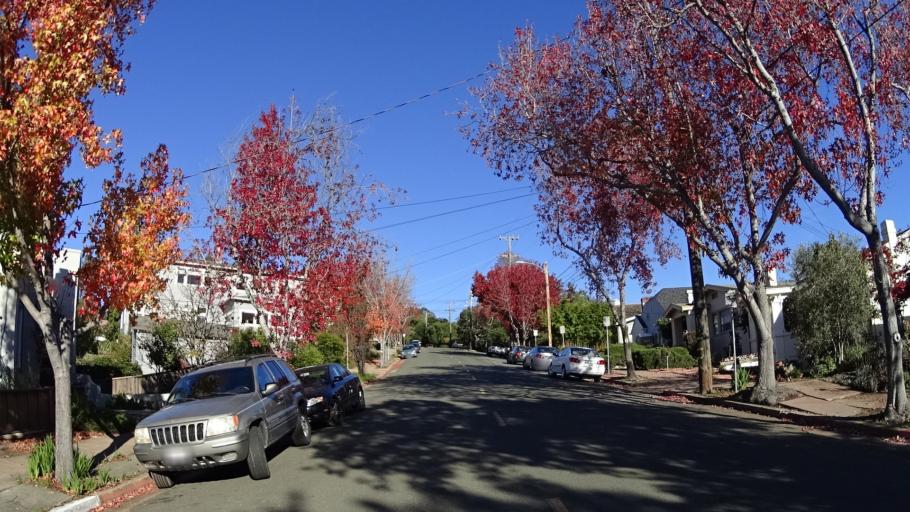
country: US
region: California
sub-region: Alameda County
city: Piedmont
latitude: 37.8201
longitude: -122.2437
